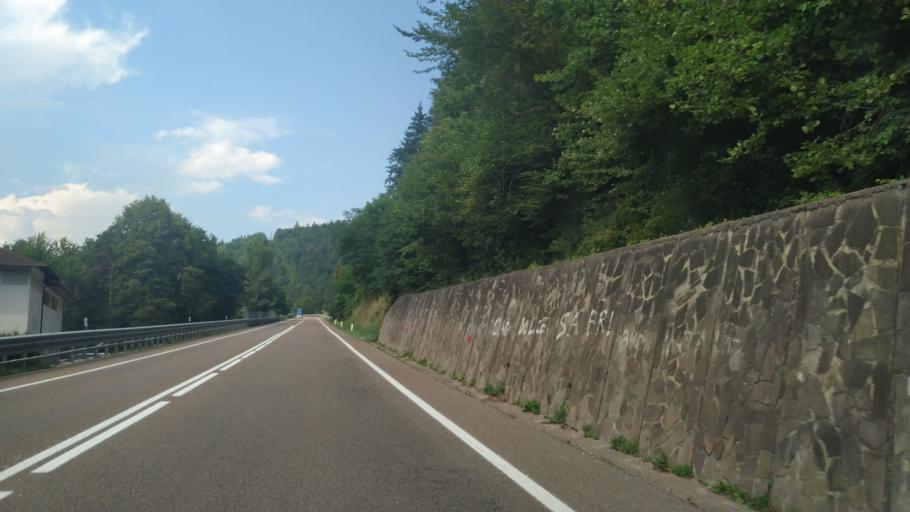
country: IT
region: Trentino-Alto Adige
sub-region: Provincia di Trento
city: Denno
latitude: 46.2735
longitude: 11.0643
